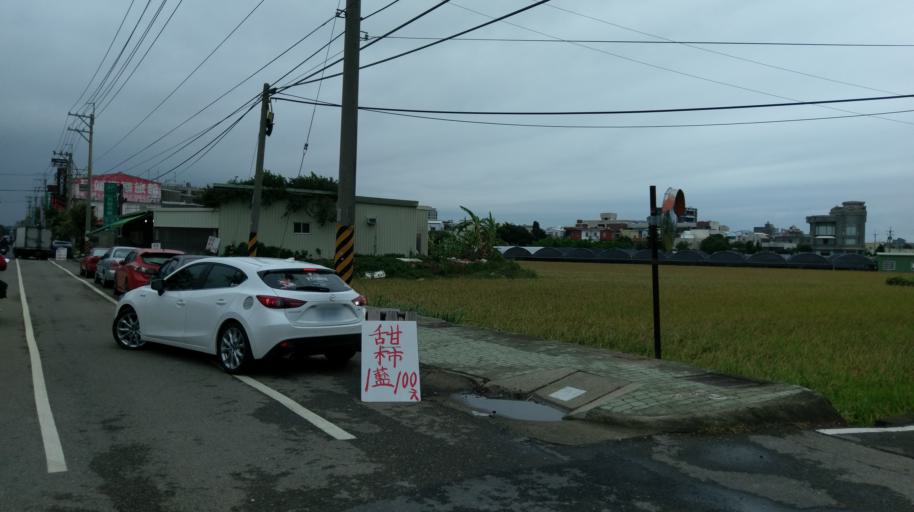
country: TW
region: Taiwan
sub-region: Hsinchu
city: Hsinchu
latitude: 24.6980
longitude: 120.9180
